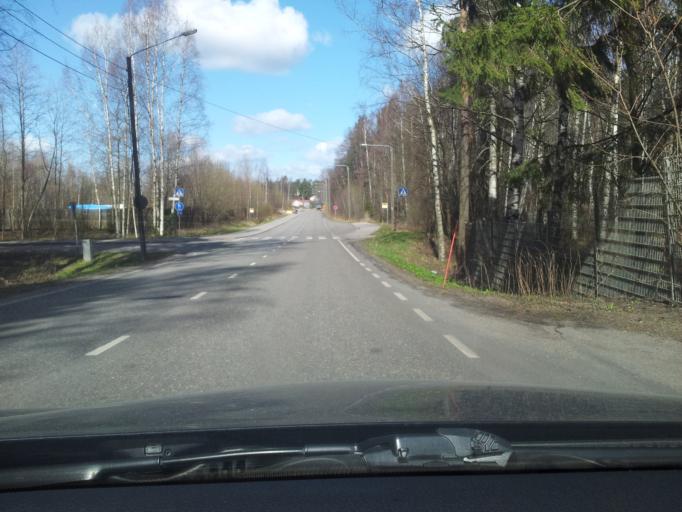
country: FI
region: Uusimaa
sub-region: Helsinki
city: Koukkuniemi
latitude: 60.1502
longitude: 24.7099
